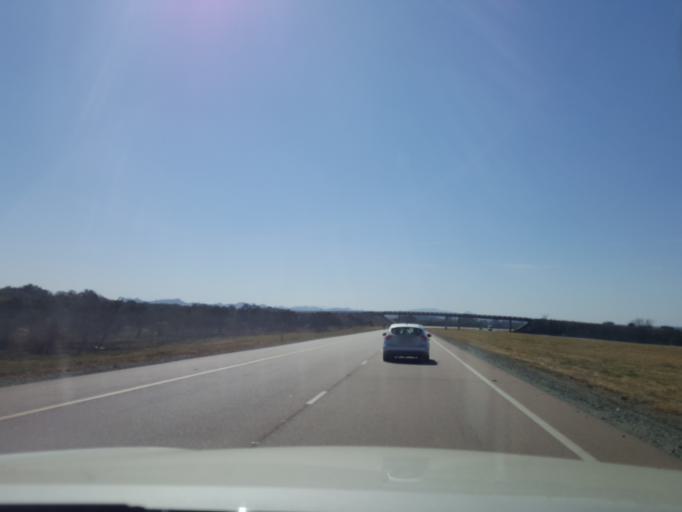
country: ZA
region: North-West
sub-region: Bojanala Platinum District Municipality
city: Brits
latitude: -25.7425
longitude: 27.5330
